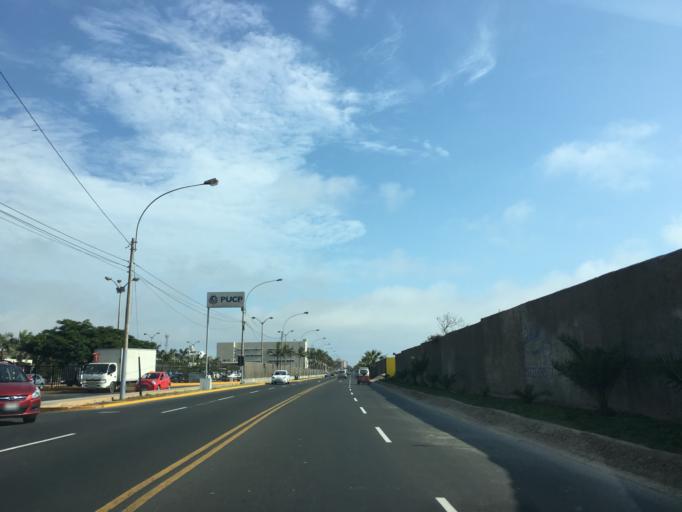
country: PE
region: Callao
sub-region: Callao
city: Callao
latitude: -12.0692
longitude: -77.0820
